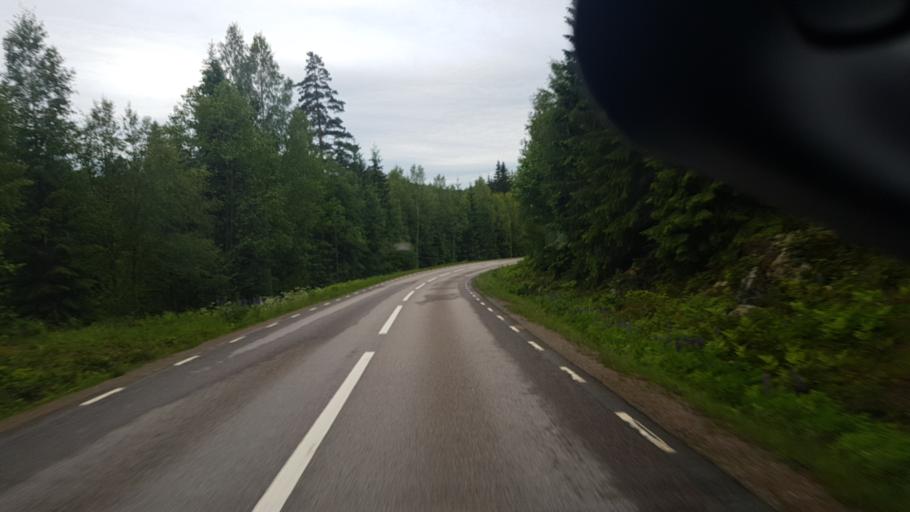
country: SE
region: Vaermland
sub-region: Eda Kommun
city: Amotfors
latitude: 59.6649
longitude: 12.3818
